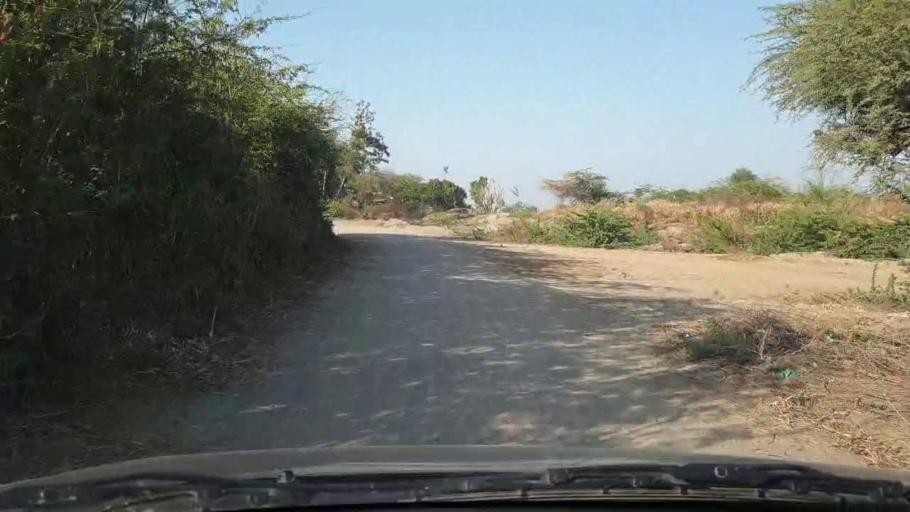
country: PK
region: Sindh
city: Samaro
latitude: 25.1603
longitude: 69.3140
